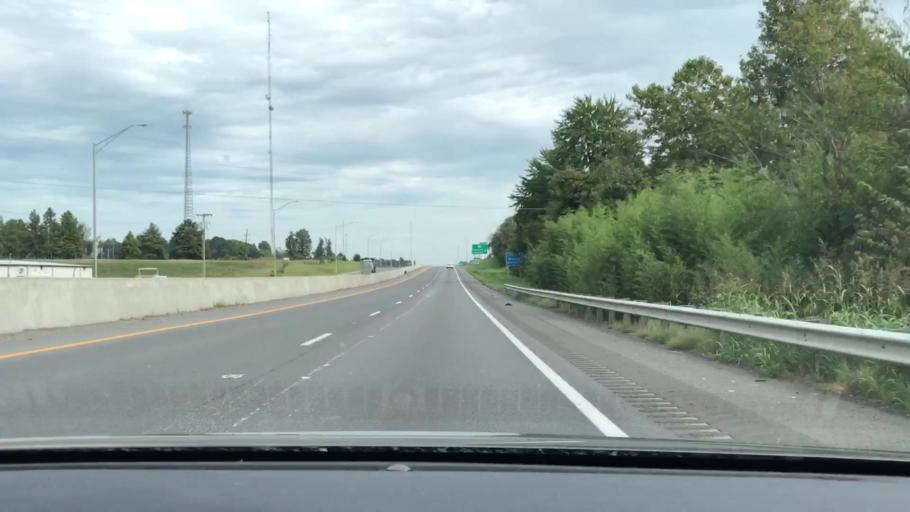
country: US
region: Kentucky
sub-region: Graves County
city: Mayfield
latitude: 36.7518
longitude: -88.6633
